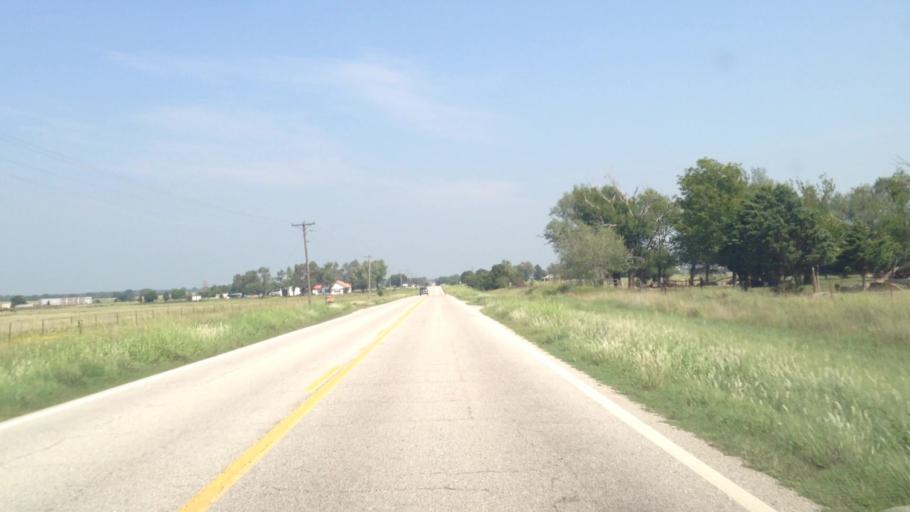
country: US
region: Oklahoma
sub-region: Craig County
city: Vinita
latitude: 36.8085
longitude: -95.1436
